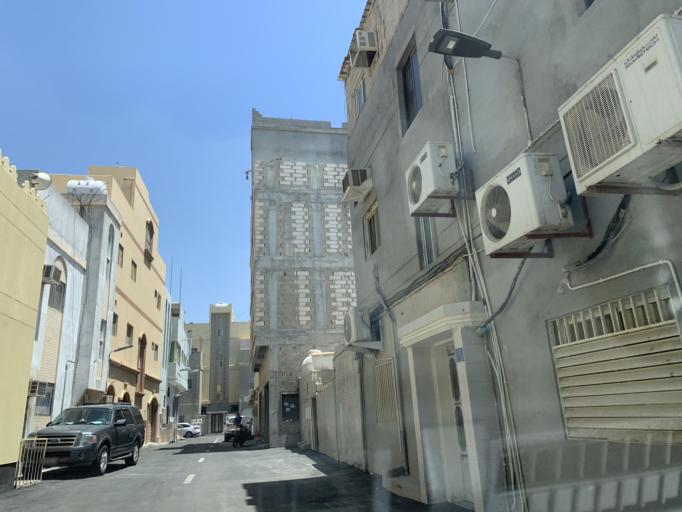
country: BH
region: Manama
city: Jidd Hafs
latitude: 26.2301
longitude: 50.4930
